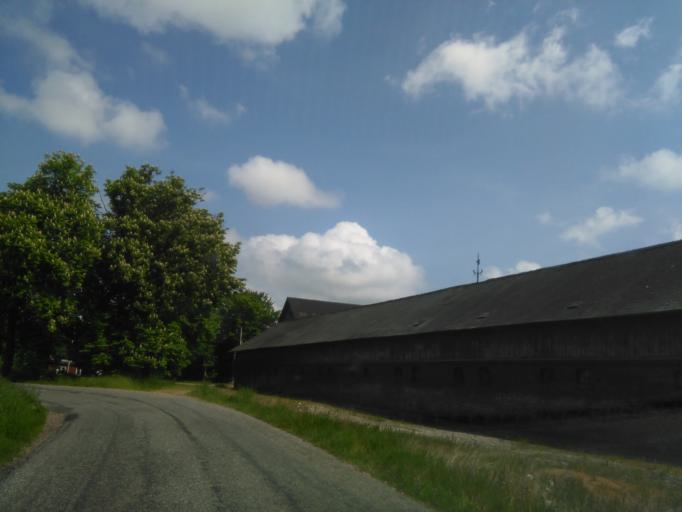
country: DK
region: Central Jutland
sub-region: Skanderborg Kommune
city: Galten
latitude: 56.2175
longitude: 9.9320
